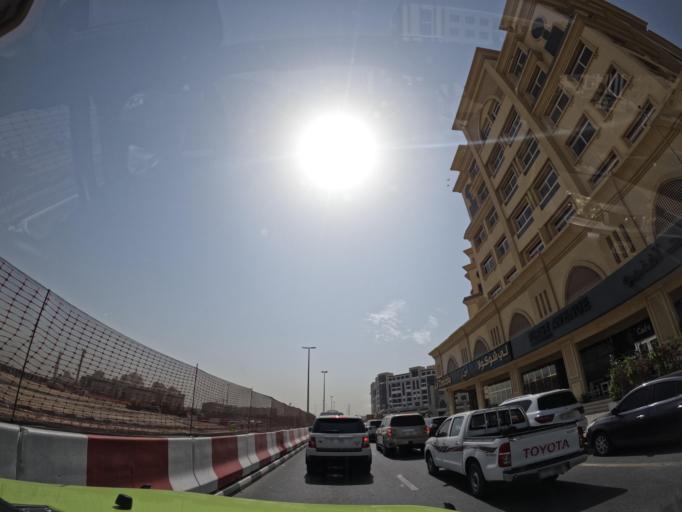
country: AE
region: Ash Shariqah
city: Sharjah
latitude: 25.3063
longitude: 55.4602
